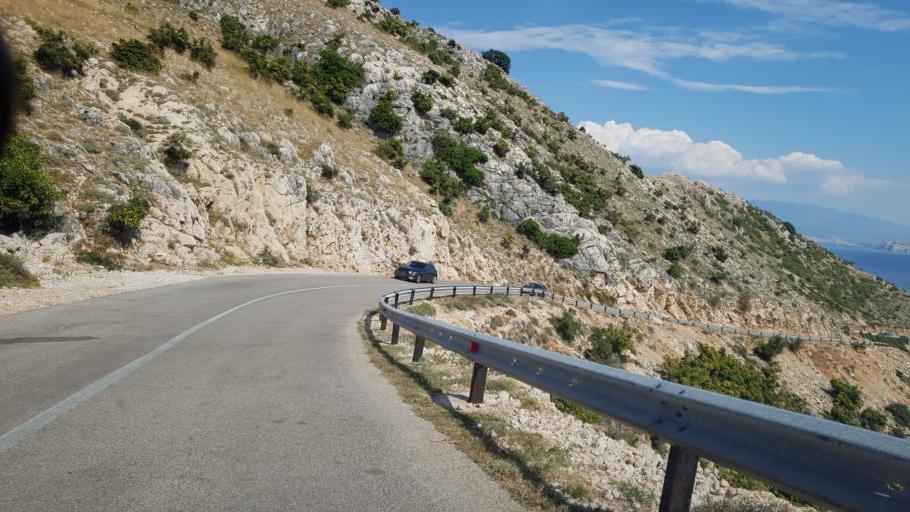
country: HR
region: Primorsko-Goranska
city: Punat
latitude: 44.9745
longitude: 14.6587
